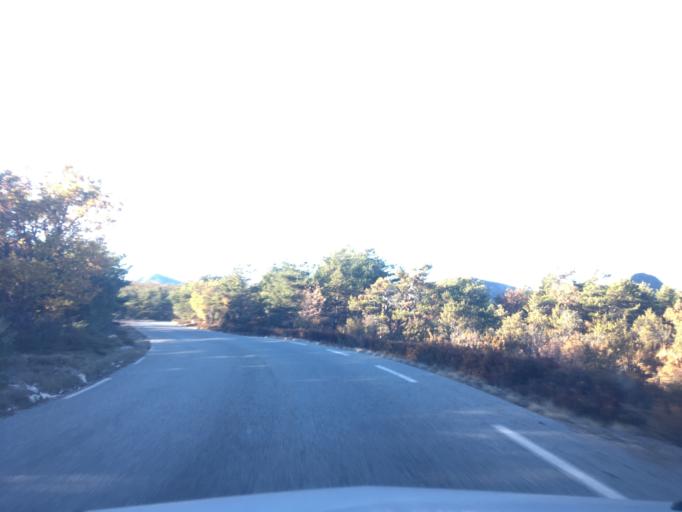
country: FR
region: Provence-Alpes-Cote d'Azur
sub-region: Departement du Var
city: Montferrat
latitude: 43.7388
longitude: 6.4304
